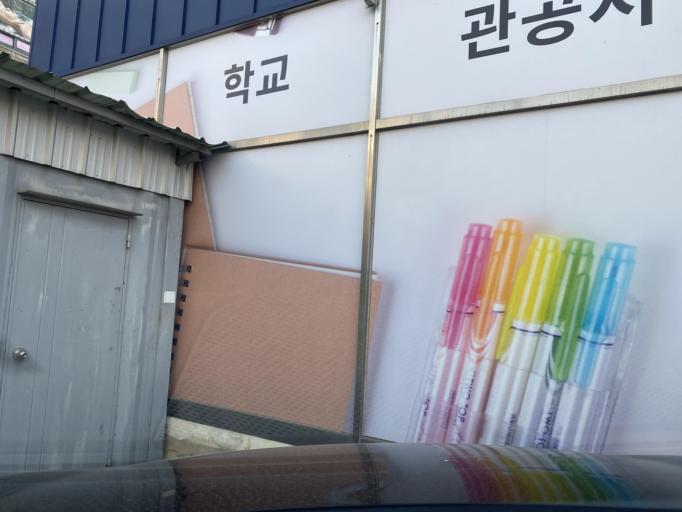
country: KR
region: Chungcheongnam-do
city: Yesan
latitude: 36.6928
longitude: 126.8301
